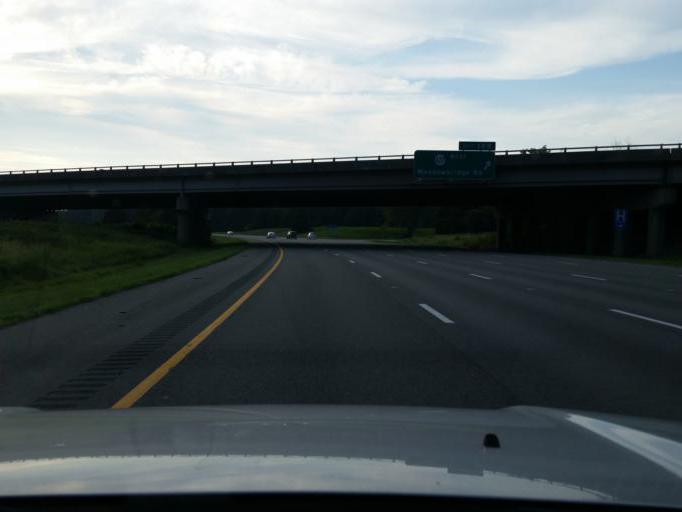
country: US
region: Virginia
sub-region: Hanover County
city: Mechanicsville
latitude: 37.6287
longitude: -77.3708
